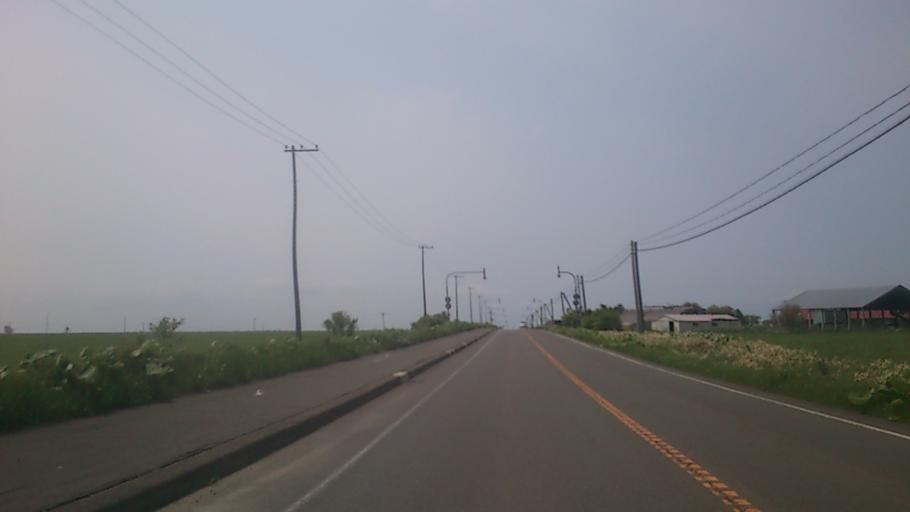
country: JP
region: Hokkaido
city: Nemuro
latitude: 43.2723
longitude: 145.5341
